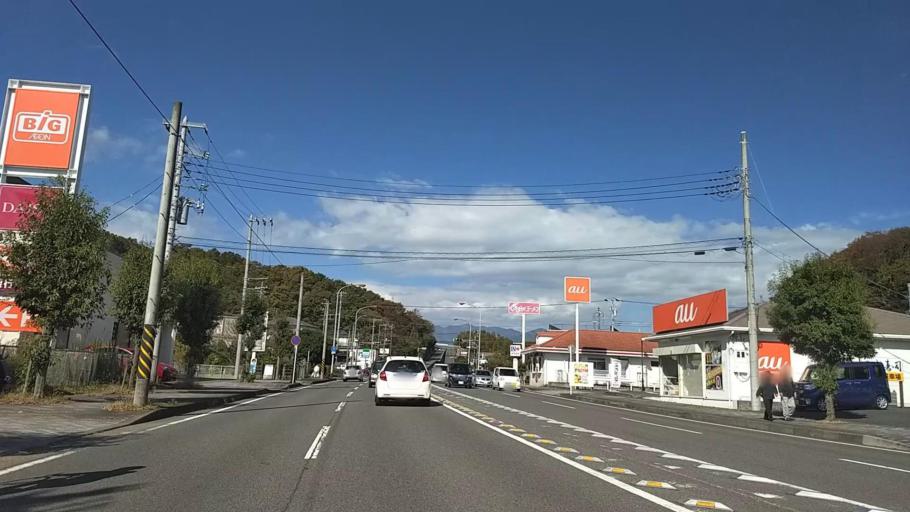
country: JP
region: Kanagawa
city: Ninomiya
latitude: 35.3154
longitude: 139.2427
